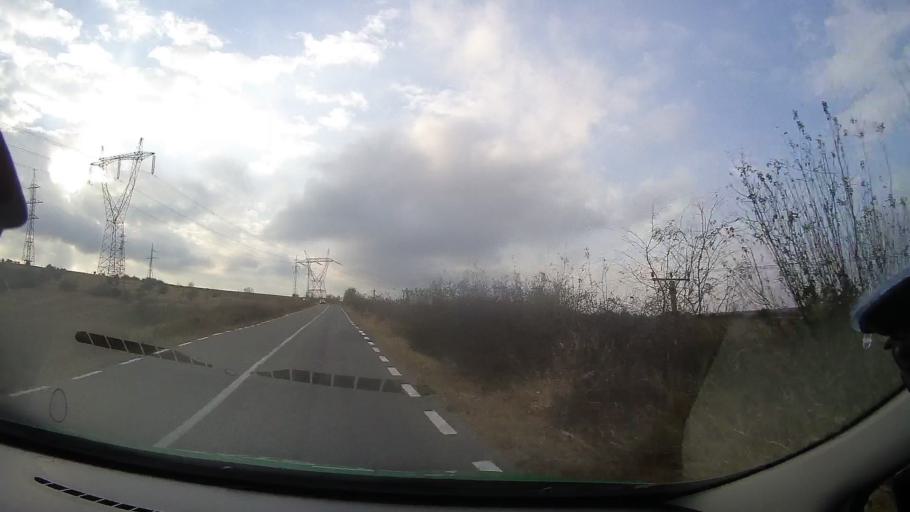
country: RO
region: Constanta
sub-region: Comuna Mircea Voda
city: Satu Nou
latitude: 44.2345
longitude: 28.2193
